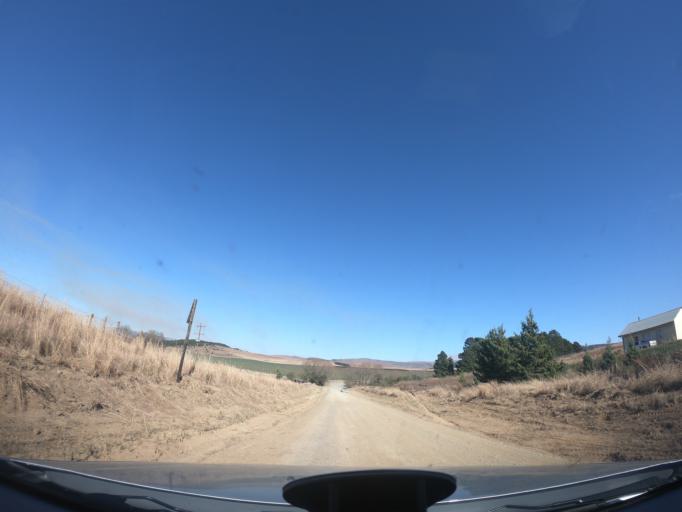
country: ZA
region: KwaZulu-Natal
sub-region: uMgungundlovu District Municipality
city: Impendle
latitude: -29.4164
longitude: 29.9292
